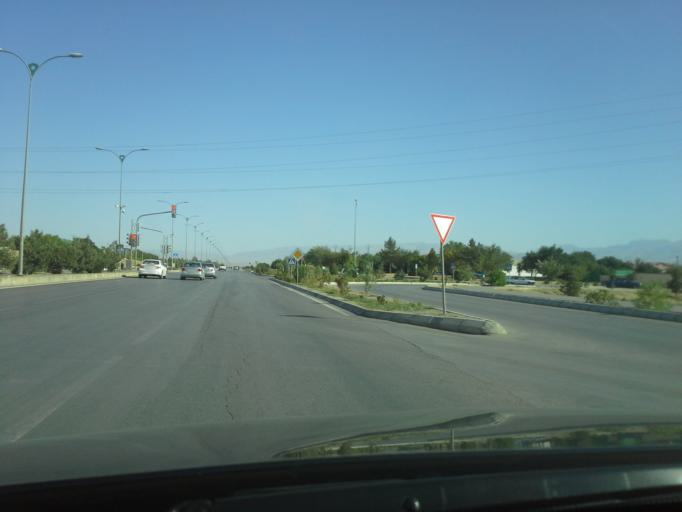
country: TM
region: Ahal
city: Ashgabat
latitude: 38.0044
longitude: 58.4042
